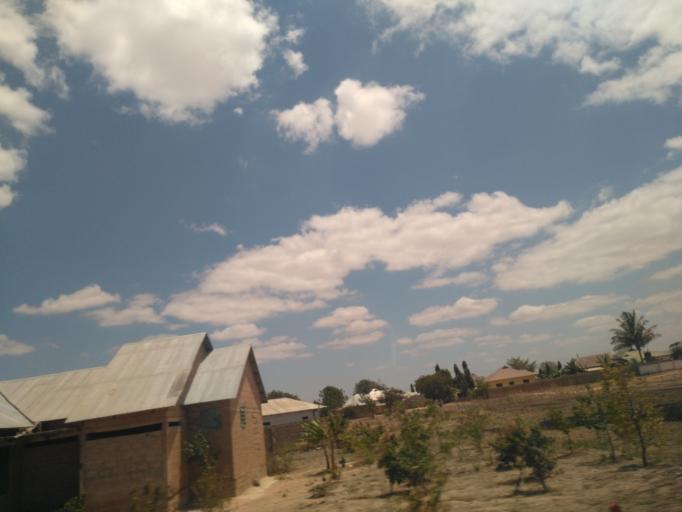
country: TZ
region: Dodoma
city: Kisasa
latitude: -6.1697
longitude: 35.7937
